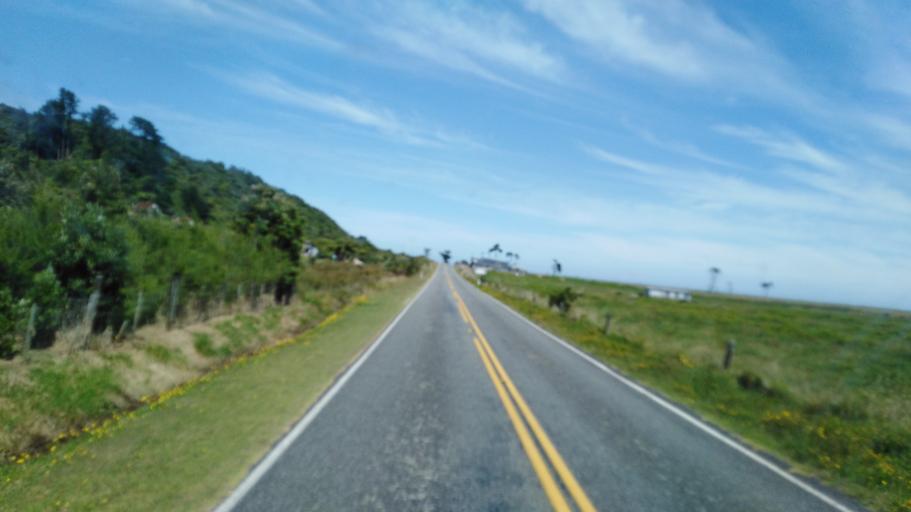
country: NZ
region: West Coast
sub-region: Buller District
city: Westport
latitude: -41.5321
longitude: 171.9391
